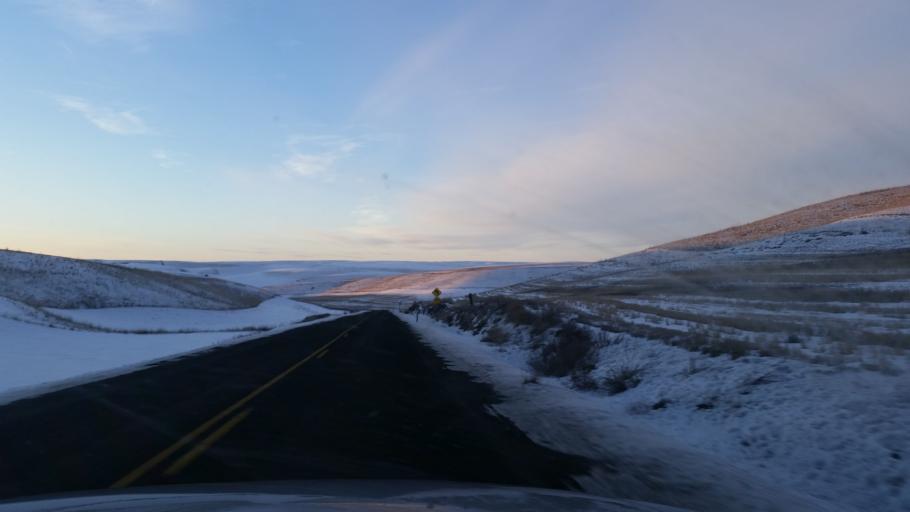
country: US
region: Washington
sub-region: Spokane County
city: Cheney
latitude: 47.1558
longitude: -117.8607
